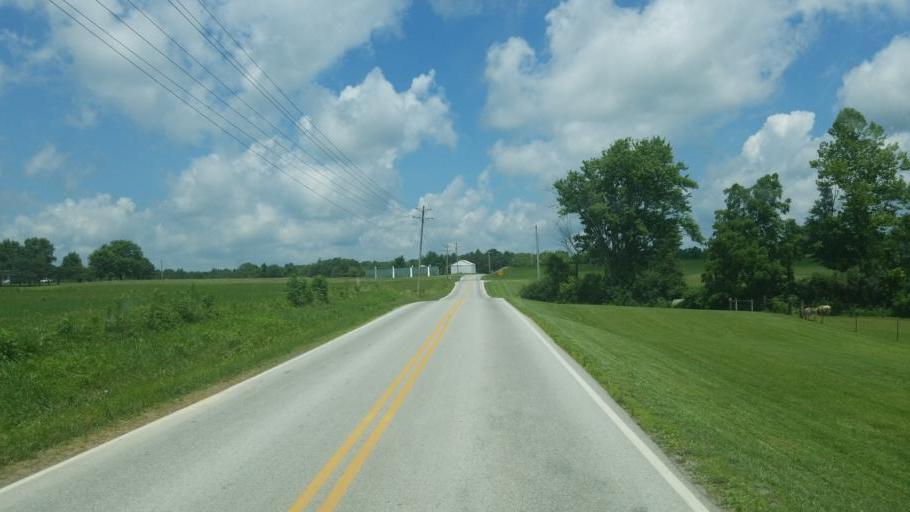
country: US
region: Ohio
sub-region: Highland County
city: Leesburg
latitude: 39.2588
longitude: -83.4740
